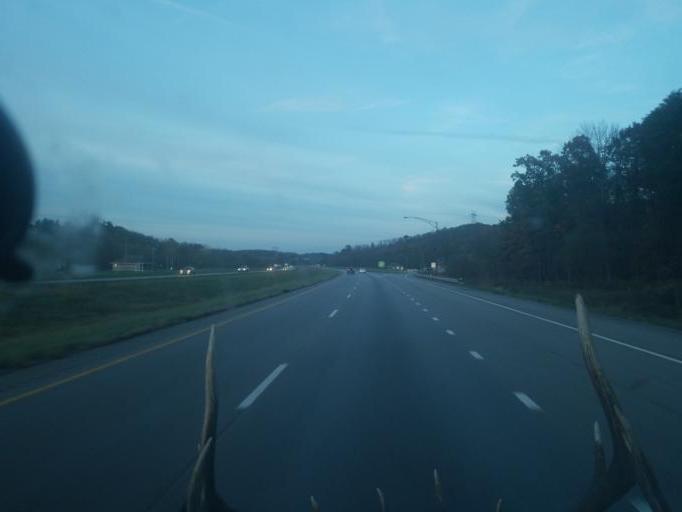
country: US
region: Ohio
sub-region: Muskingum County
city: New Concord
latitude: 39.9936
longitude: -81.6700
